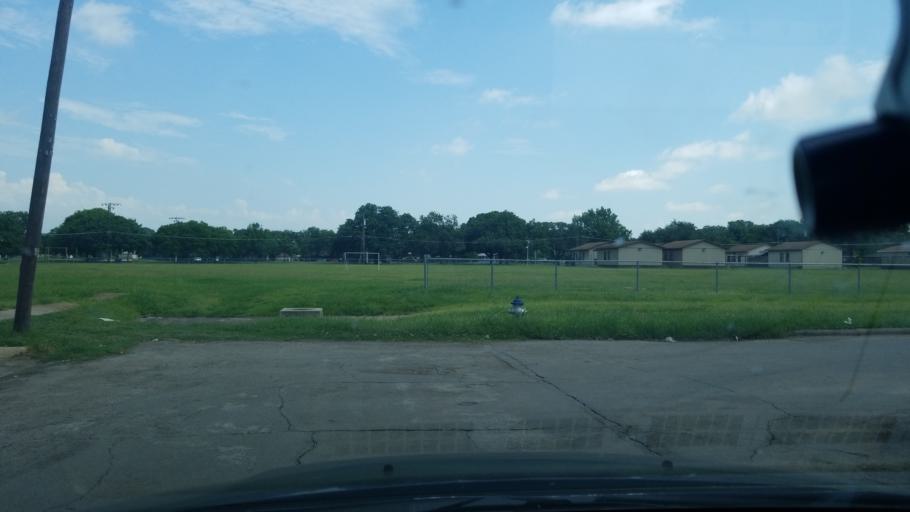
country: US
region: Texas
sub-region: Dallas County
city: Balch Springs
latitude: 32.7414
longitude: -96.6902
